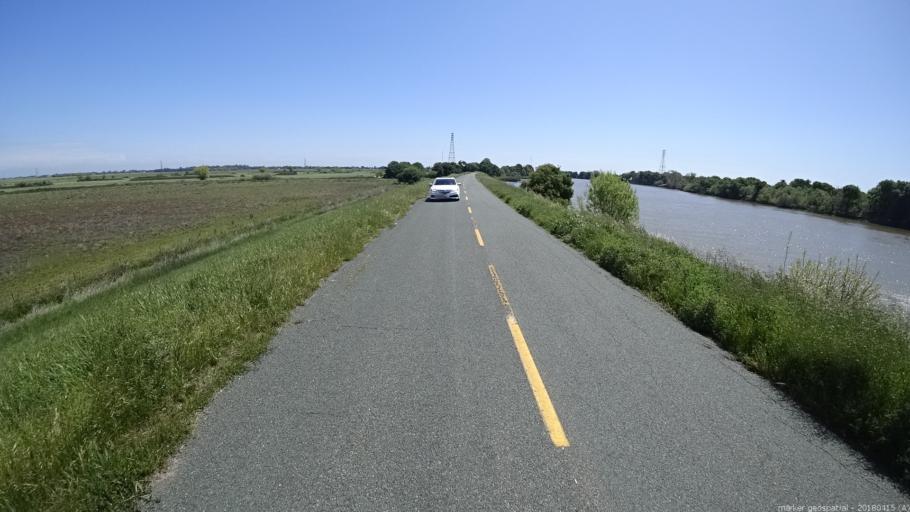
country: US
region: California
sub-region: Solano County
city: Rio Vista
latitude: 38.1718
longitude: -121.6331
